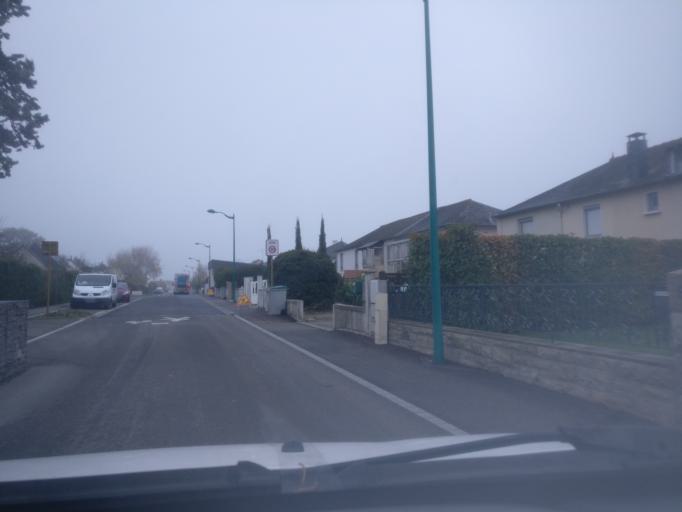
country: FR
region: Brittany
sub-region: Departement d'Ille-et-Vilaine
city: Chartres-de-Bretagne
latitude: 48.0084
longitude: -1.7029
